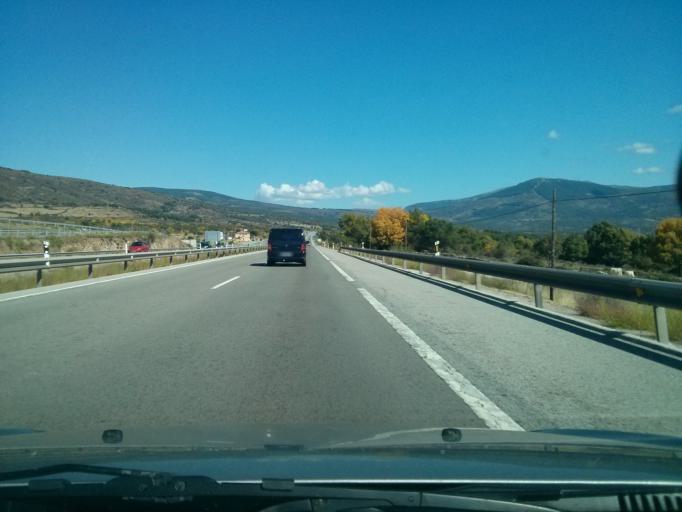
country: ES
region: Madrid
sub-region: Provincia de Madrid
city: Braojos
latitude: 41.0411
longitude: -3.6167
